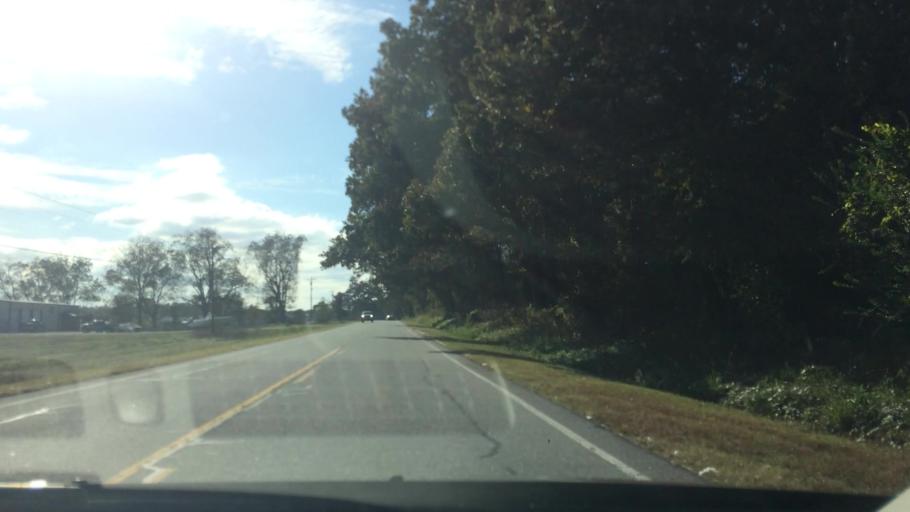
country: US
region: North Carolina
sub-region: Greene County
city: Snow Hill
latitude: 35.4584
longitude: -77.7077
